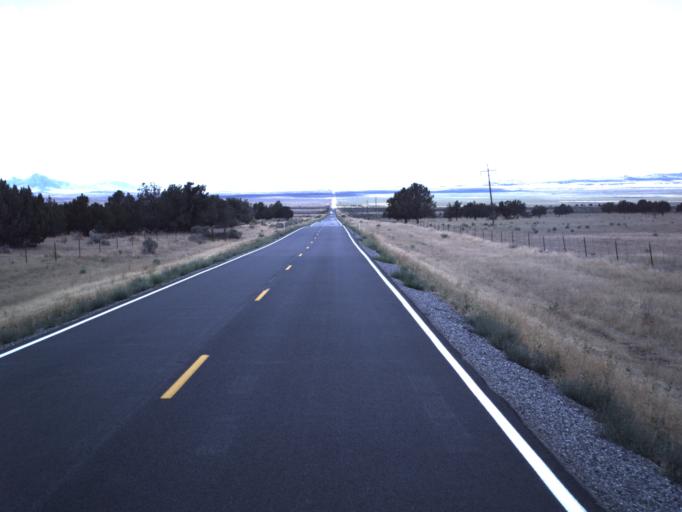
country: US
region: Utah
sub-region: Tooele County
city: Grantsville
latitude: 40.3095
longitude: -112.6392
